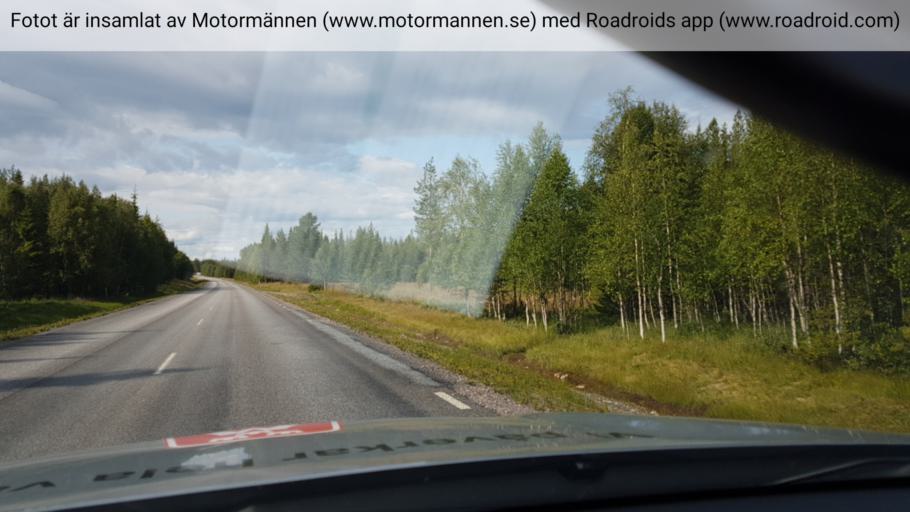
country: SE
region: Norrbotten
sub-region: Arvidsjaurs Kommun
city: Arvidsjaur
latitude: 65.5890
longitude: 19.4595
